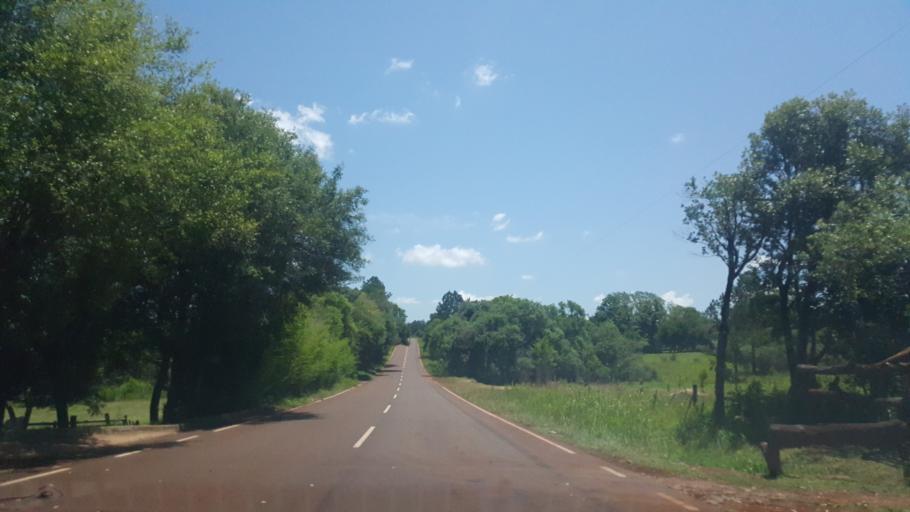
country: AR
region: Misiones
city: Garupa
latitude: -27.5043
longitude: -55.8533
